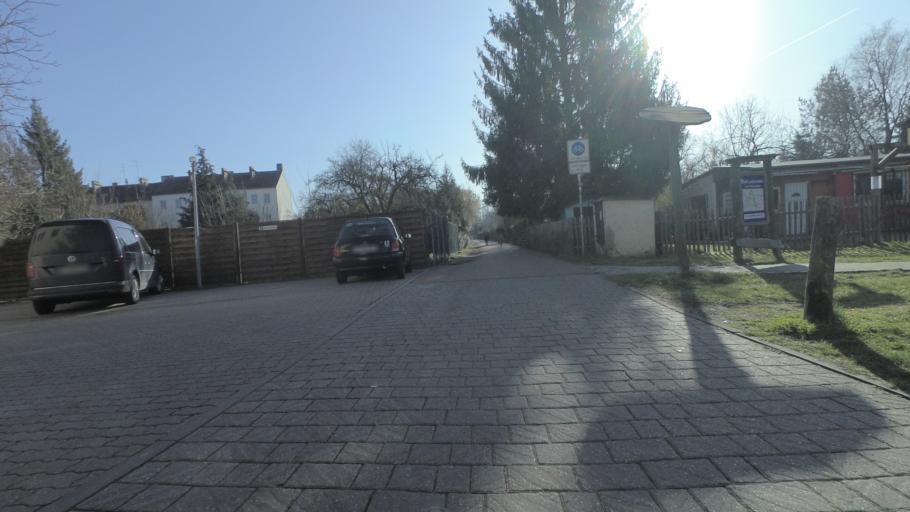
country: DE
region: Brandenburg
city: Luckenwalde
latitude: 52.0855
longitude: 13.1707
